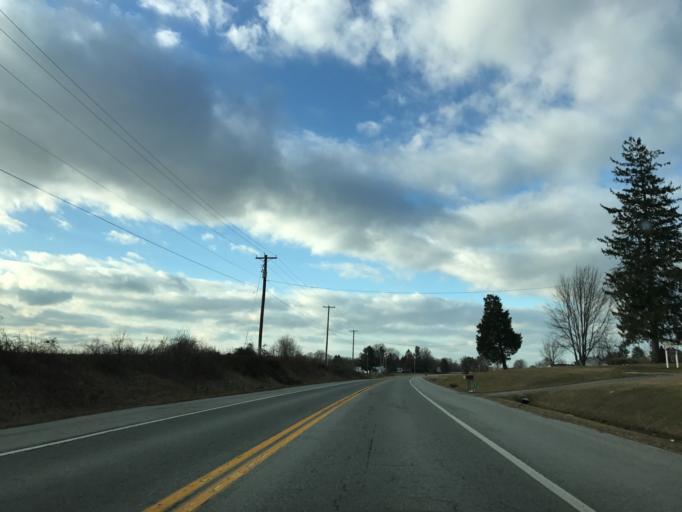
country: US
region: Maryland
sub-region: Cecil County
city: Rising Sun
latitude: 39.6801
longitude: -76.0342
